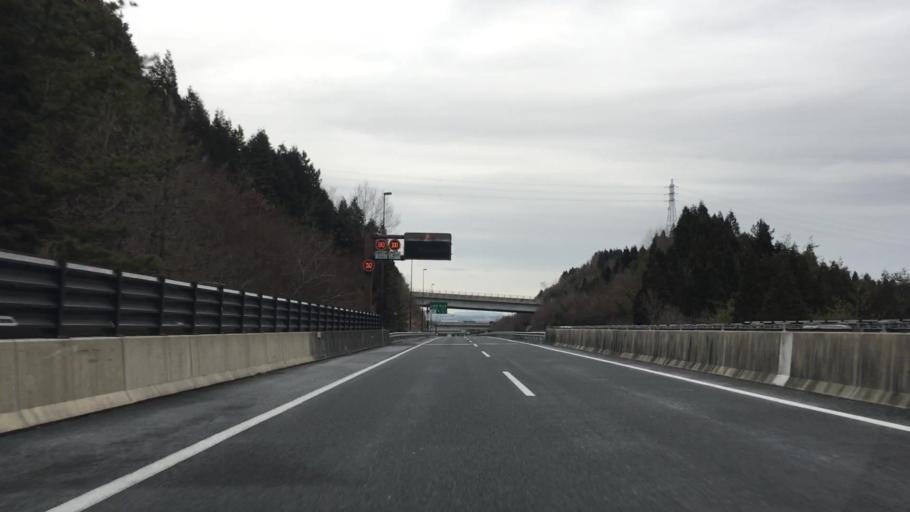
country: JP
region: Gifu
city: Toki
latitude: 35.3276
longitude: 137.1756
